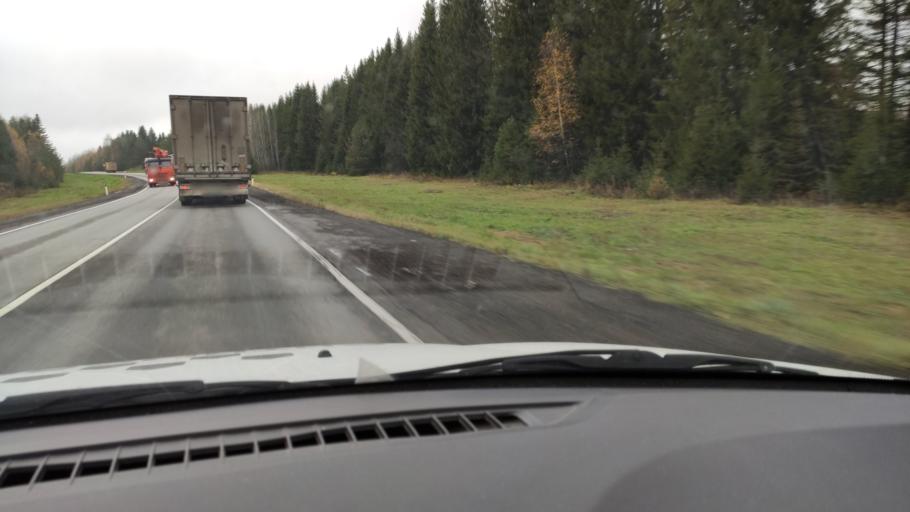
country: RU
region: Kirov
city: Belaya Kholunitsa
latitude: 58.8168
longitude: 50.5930
